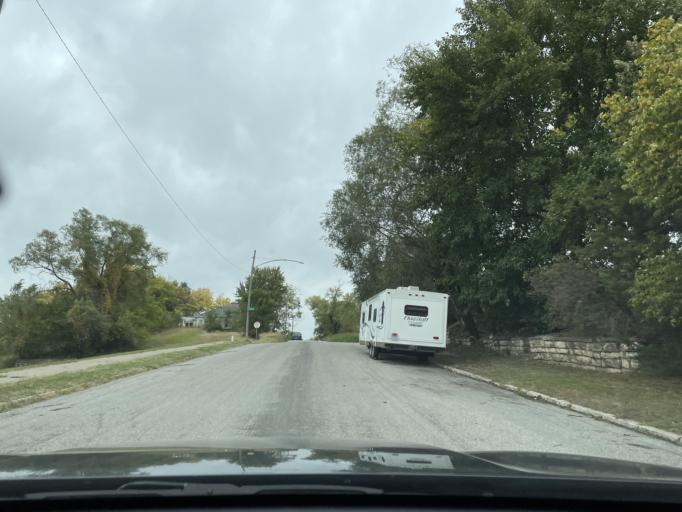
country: US
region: Missouri
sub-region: Buchanan County
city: Saint Joseph
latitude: 39.7733
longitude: -94.8541
